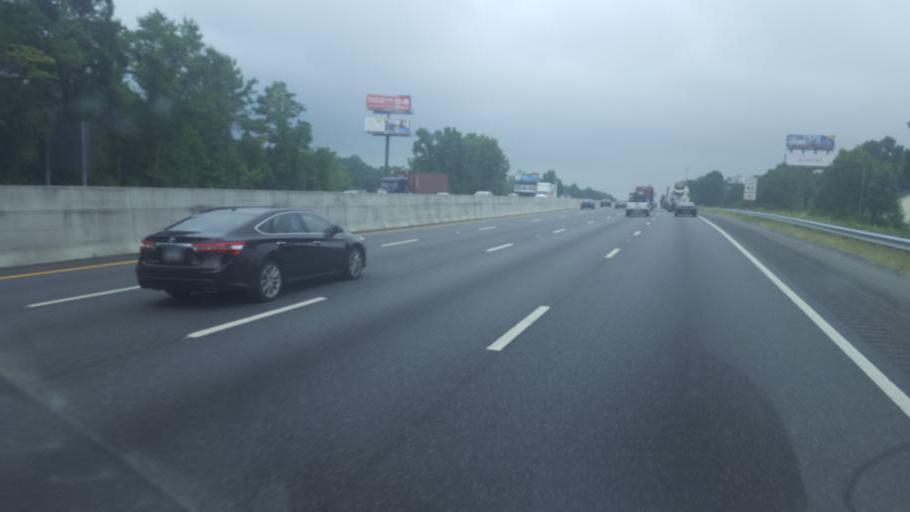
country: US
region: South Carolina
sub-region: York County
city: Fort Mill
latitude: 35.0074
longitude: -80.9711
